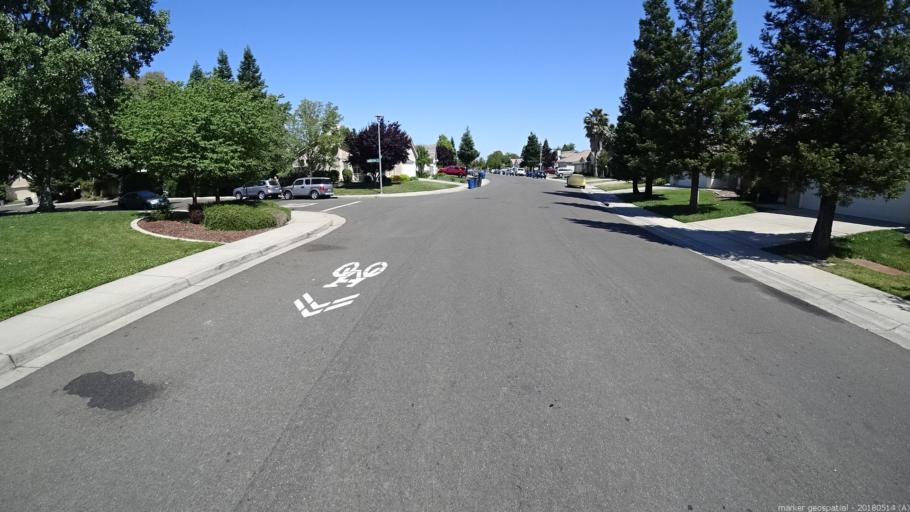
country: US
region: California
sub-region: Yolo County
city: West Sacramento
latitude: 38.6389
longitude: -121.5302
